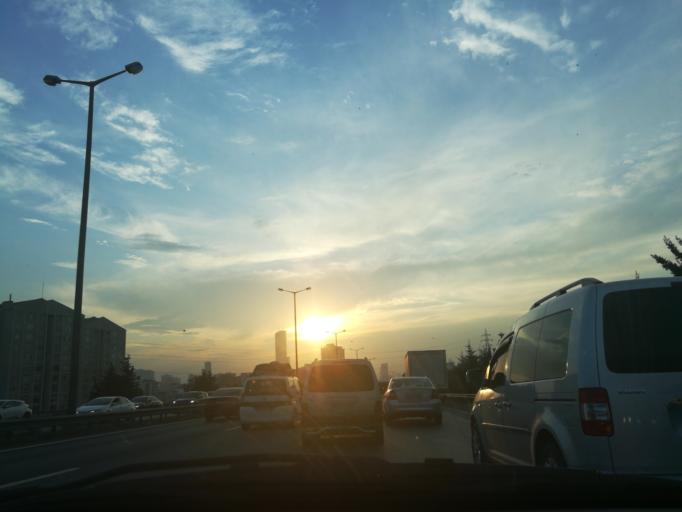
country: TR
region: Istanbul
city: Umraniye
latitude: 40.9951
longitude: 29.1492
